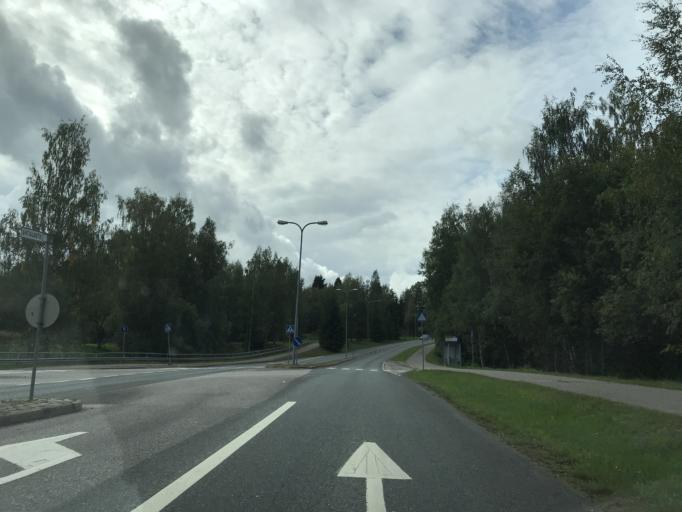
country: FI
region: Paijanne Tavastia
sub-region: Lahti
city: Lahti
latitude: 60.9930
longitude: 25.7467
